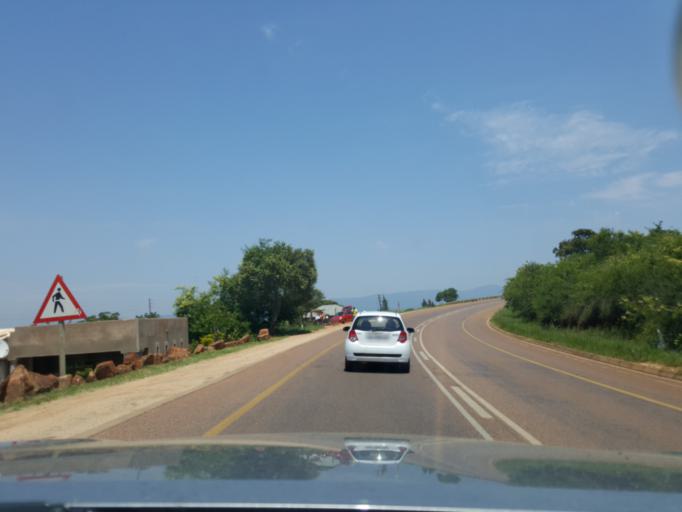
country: ZA
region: Limpopo
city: Thulamahashi
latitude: -24.9190
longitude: 31.1230
